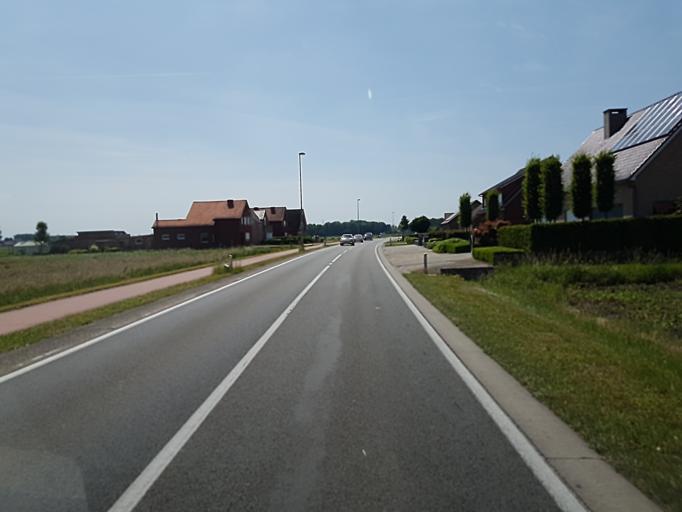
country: BE
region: Flanders
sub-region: Provincie Antwerpen
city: Retie
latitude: 51.2820
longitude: 5.0911
